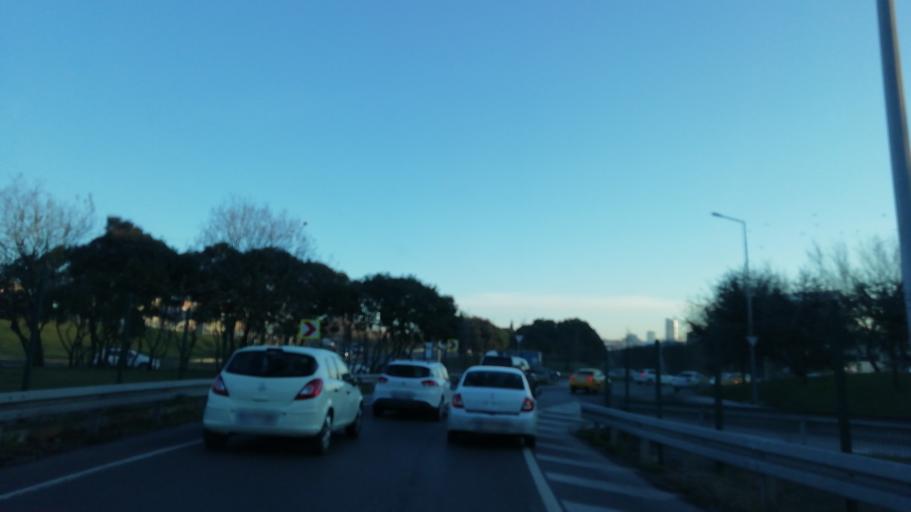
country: TR
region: Istanbul
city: Sisli
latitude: 41.0550
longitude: 28.9612
